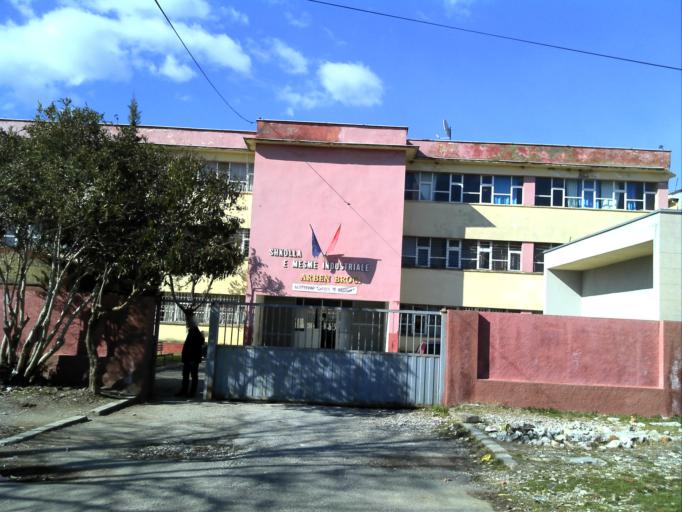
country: AL
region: Shkoder
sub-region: Rrethi i Shkodres
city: Shkoder
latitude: 42.0779
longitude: 19.5267
